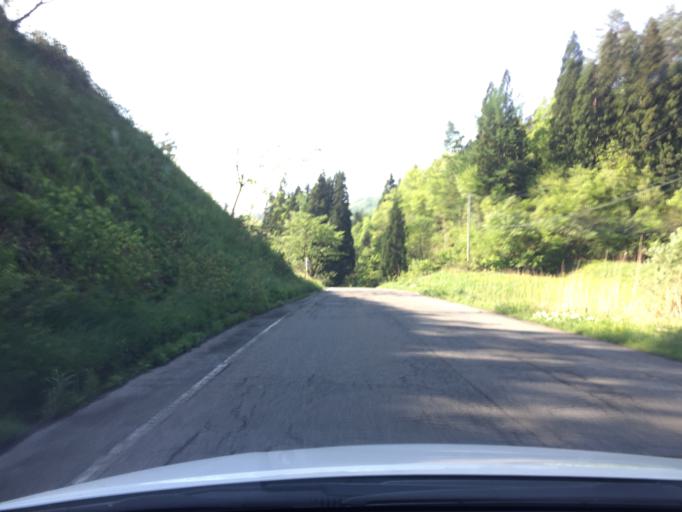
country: JP
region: Fukushima
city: Kitakata
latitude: 37.6690
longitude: 139.6148
